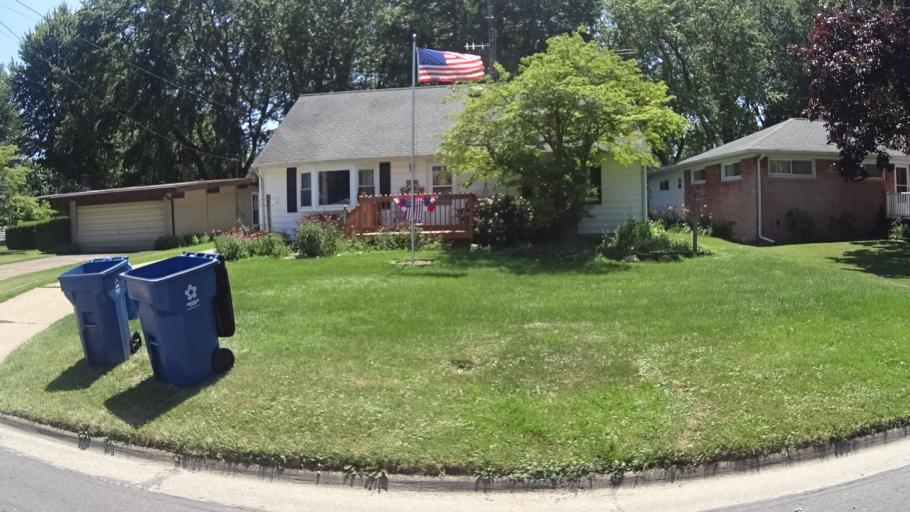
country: US
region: Ohio
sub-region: Erie County
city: Huron
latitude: 41.3916
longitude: -82.5657
